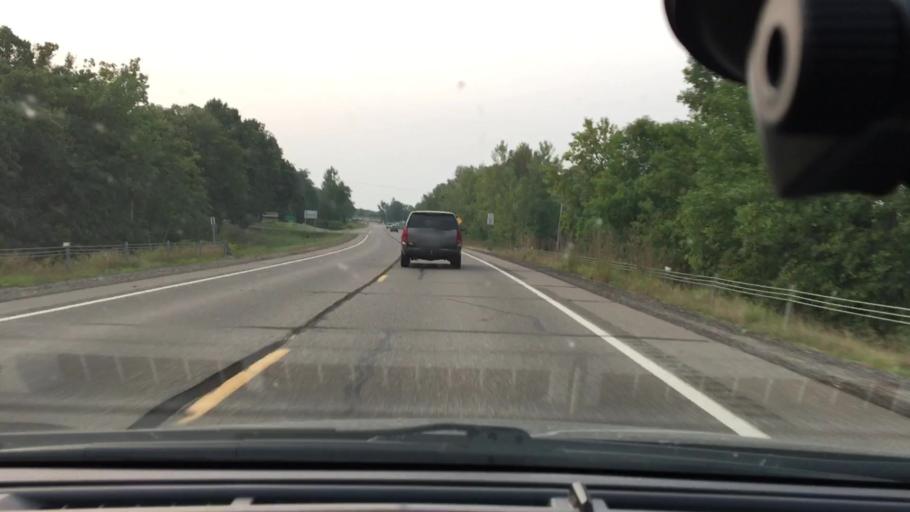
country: US
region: Minnesota
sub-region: Crow Wing County
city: Crosby
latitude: 46.4688
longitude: -93.8876
